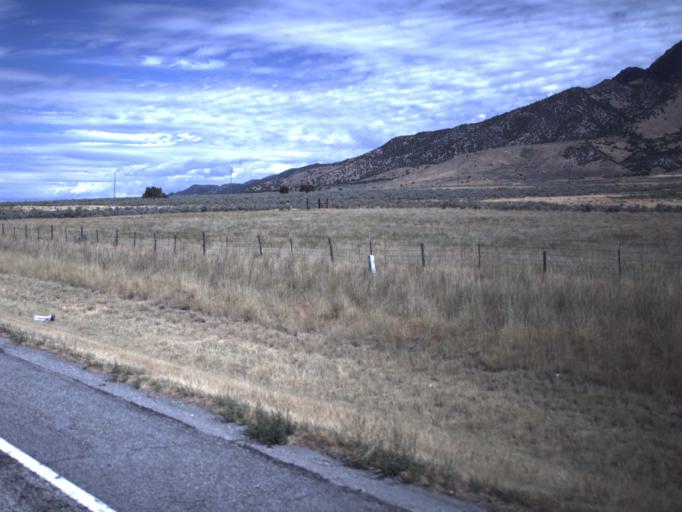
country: US
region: Utah
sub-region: Box Elder County
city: Garland
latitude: 41.8805
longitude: -112.1551
